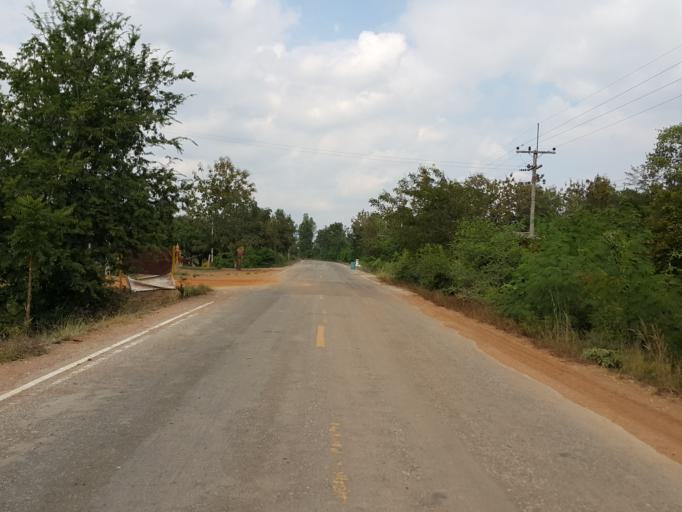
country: TH
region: Sukhothai
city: Thung Saliam
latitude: 17.3742
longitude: 99.5923
